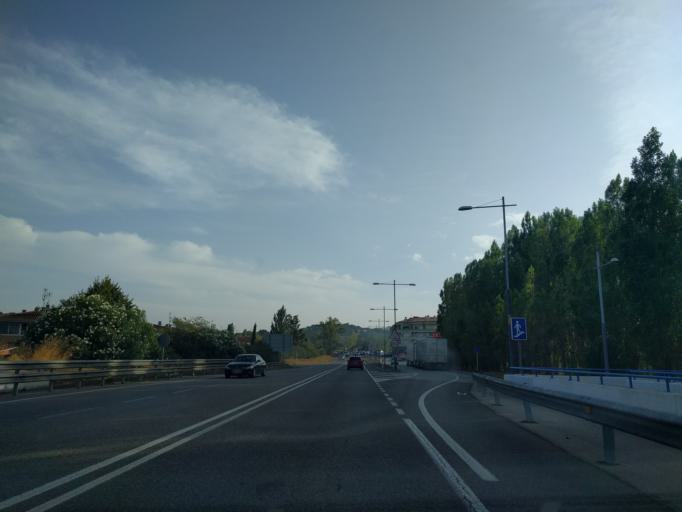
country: ES
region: Catalonia
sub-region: Provincia de Barcelona
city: Tordera
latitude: 41.6951
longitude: 2.7250
